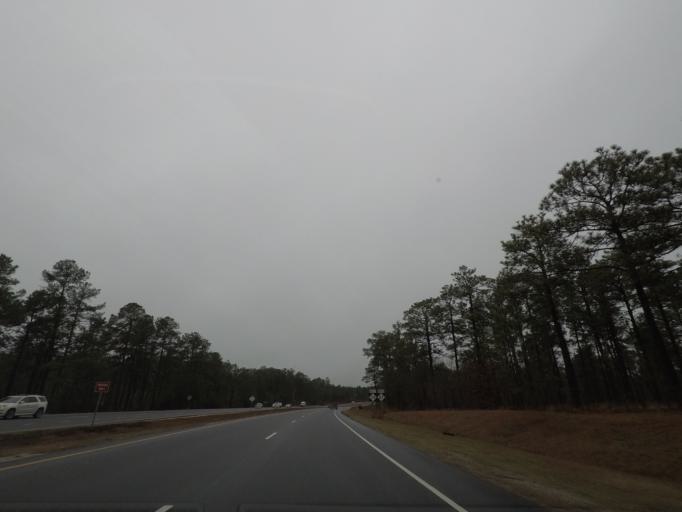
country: US
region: North Carolina
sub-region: Cumberland County
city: Spring Lake
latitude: 35.2318
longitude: -79.0169
